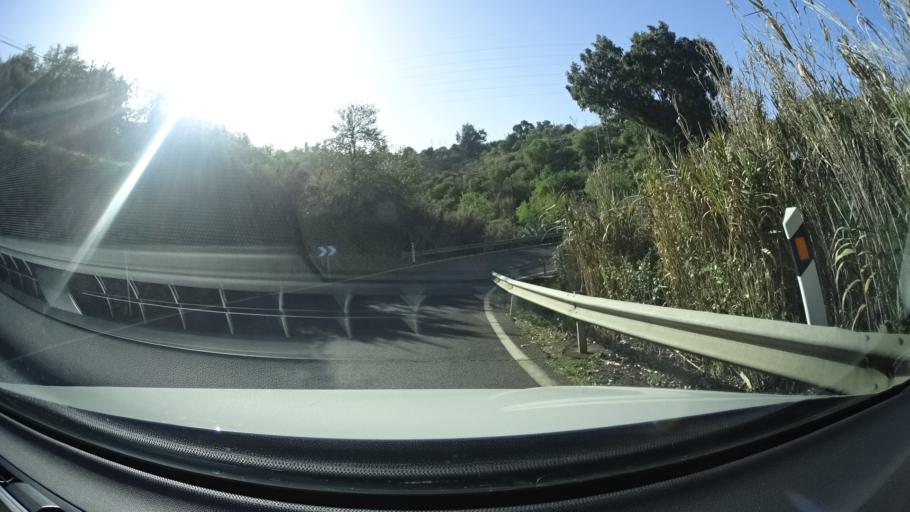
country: ES
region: Canary Islands
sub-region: Provincia de Las Palmas
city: Vega de San Mateo
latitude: 28.0178
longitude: -15.5410
